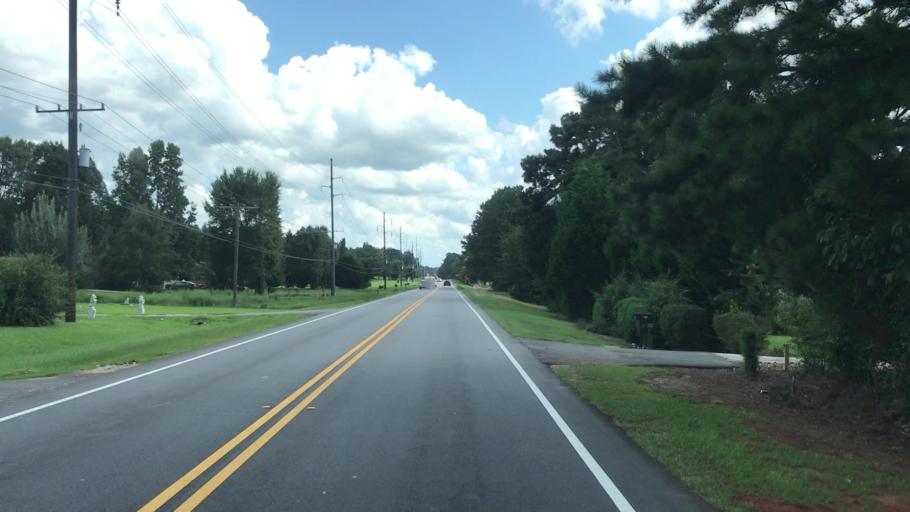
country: US
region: Georgia
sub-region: Newton County
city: Oxford
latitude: 33.6442
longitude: -83.8353
